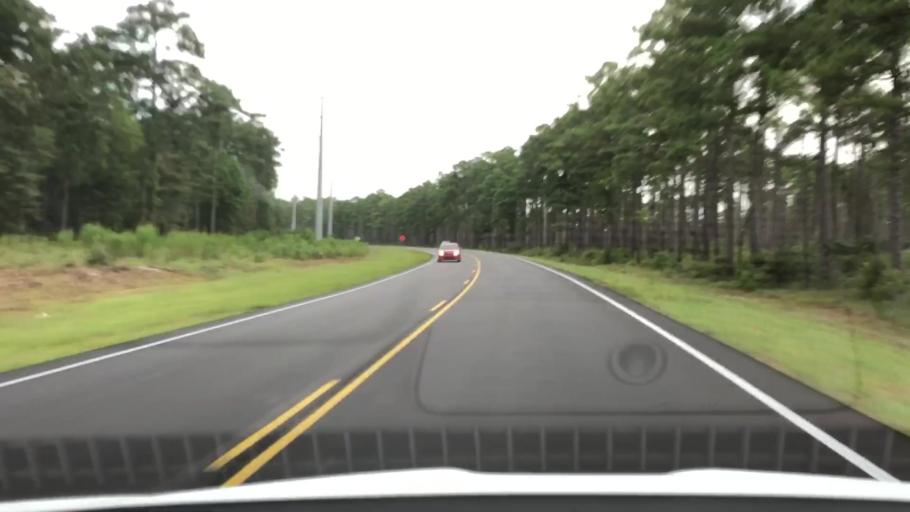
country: US
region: North Carolina
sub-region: Onslow County
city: Swansboro
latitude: 34.7717
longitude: -77.0976
